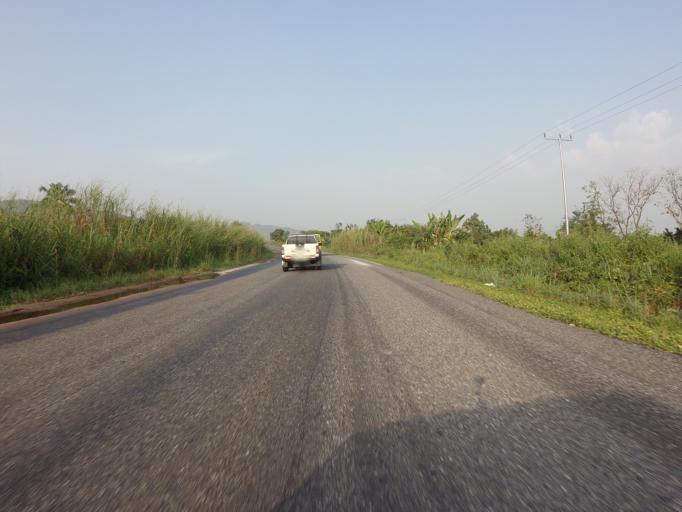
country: GH
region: Volta
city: Ho
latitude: 6.4792
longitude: 0.2322
